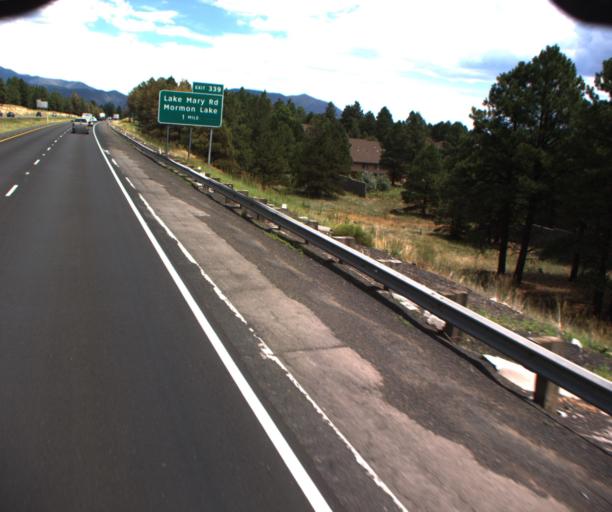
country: US
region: Arizona
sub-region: Coconino County
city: Flagstaff
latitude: 35.1525
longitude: -111.6805
